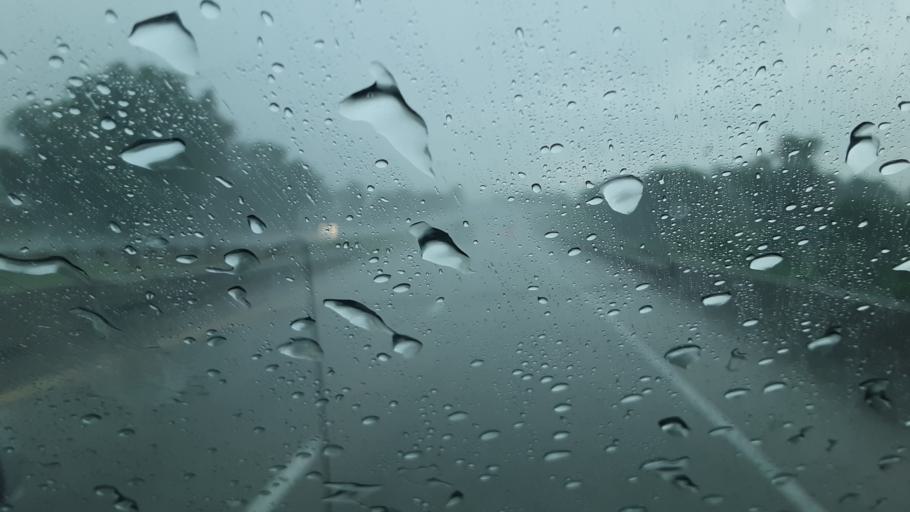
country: US
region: Iowa
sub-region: Pottawattamie County
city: Council Bluffs
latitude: 41.2610
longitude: -95.8028
